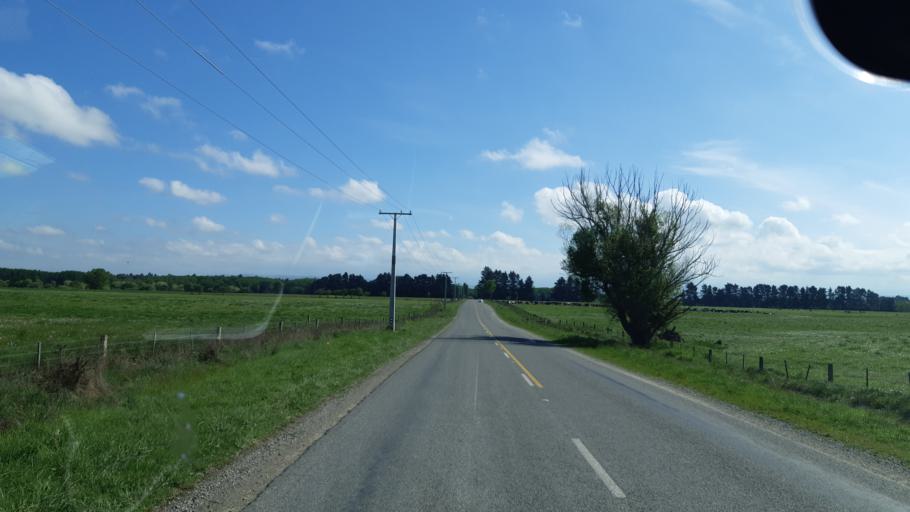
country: NZ
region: Canterbury
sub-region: Timaru District
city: Pleasant Point
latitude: -44.2429
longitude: 171.1573
